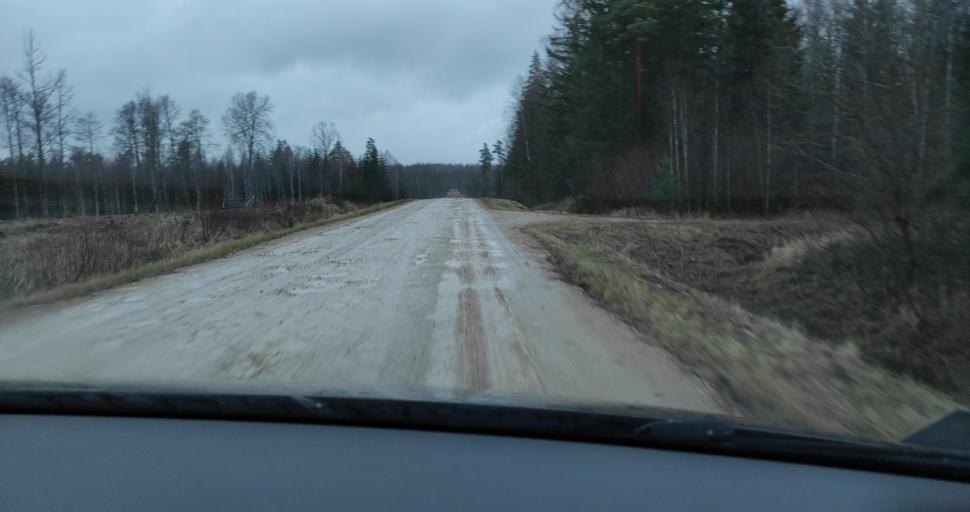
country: LV
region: Skrunda
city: Skrunda
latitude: 56.5638
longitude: 22.1315
